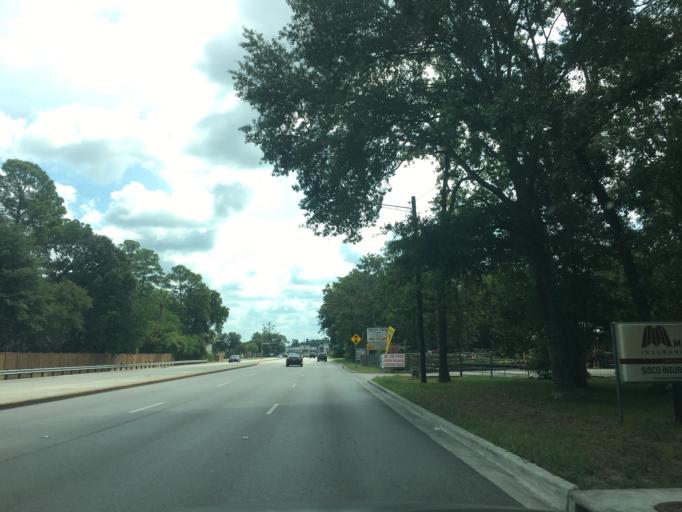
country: US
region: Texas
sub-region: Harris County
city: Spring
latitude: 30.1239
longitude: -95.4130
